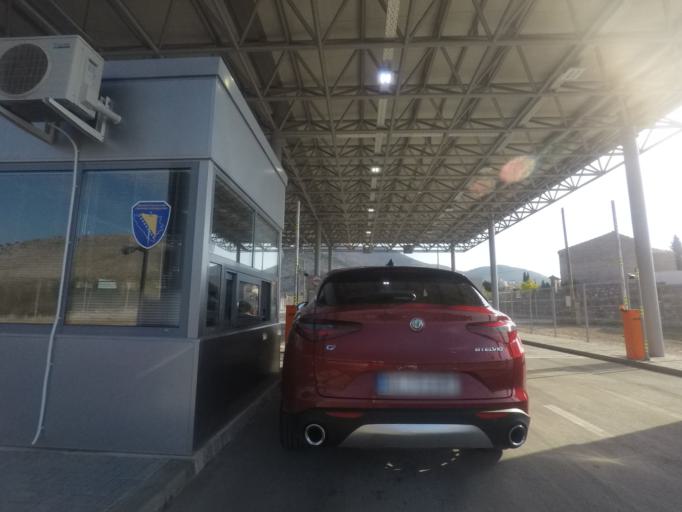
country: HR
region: Dubrovacko-Neretvanska
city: Cibaca
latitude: 42.6590
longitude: 18.1627
